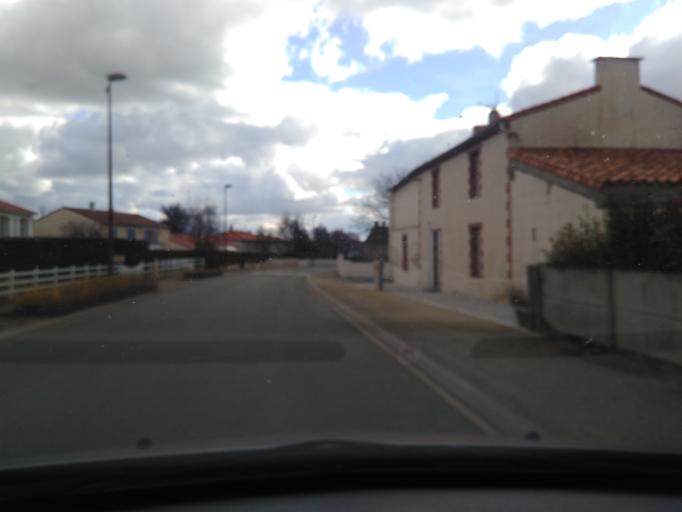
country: FR
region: Pays de la Loire
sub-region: Departement de la Vendee
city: Saint-Martin-des-Noyers
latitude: 46.7259
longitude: -1.1798
